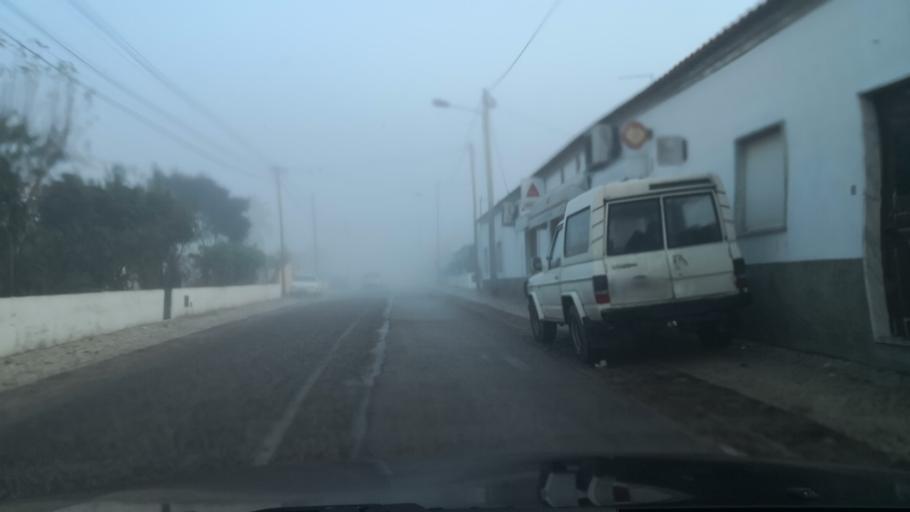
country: PT
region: Setubal
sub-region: Palmela
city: Palmela
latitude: 38.5685
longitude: -8.8350
